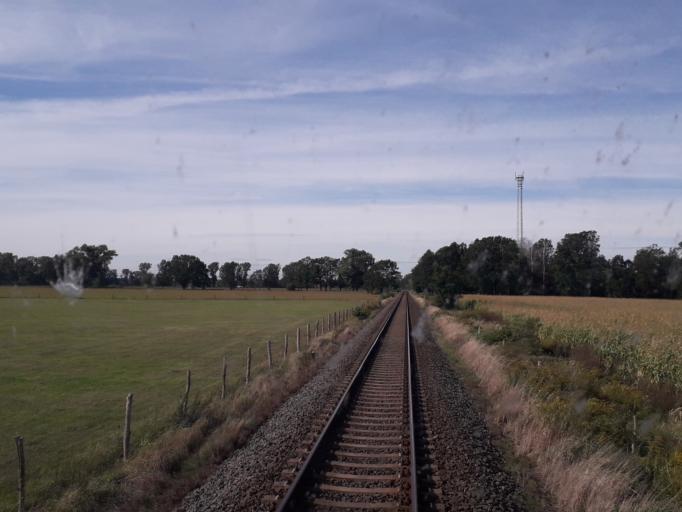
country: DE
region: Brandenburg
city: Kremmen
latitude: 52.7965
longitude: 13.0330
